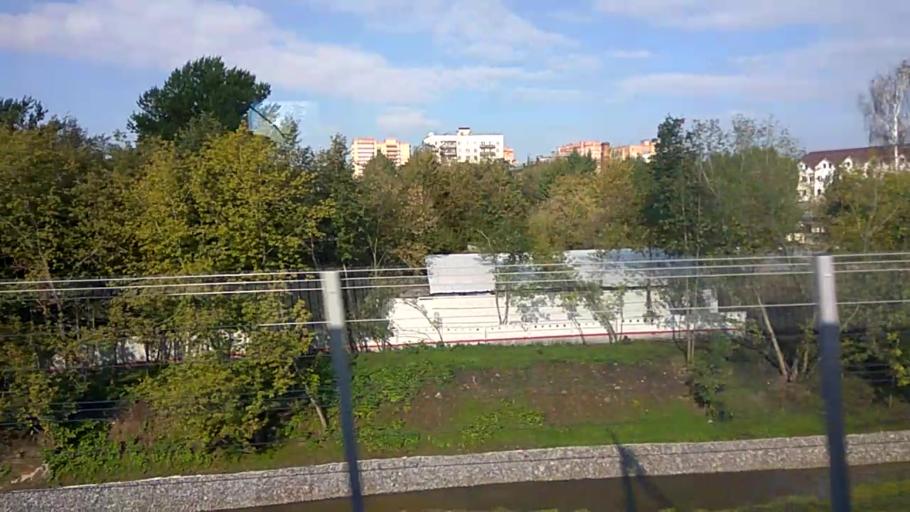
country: RU
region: Moscow
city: Tekstil'shchiki
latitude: 55.7273
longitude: 37.7245
